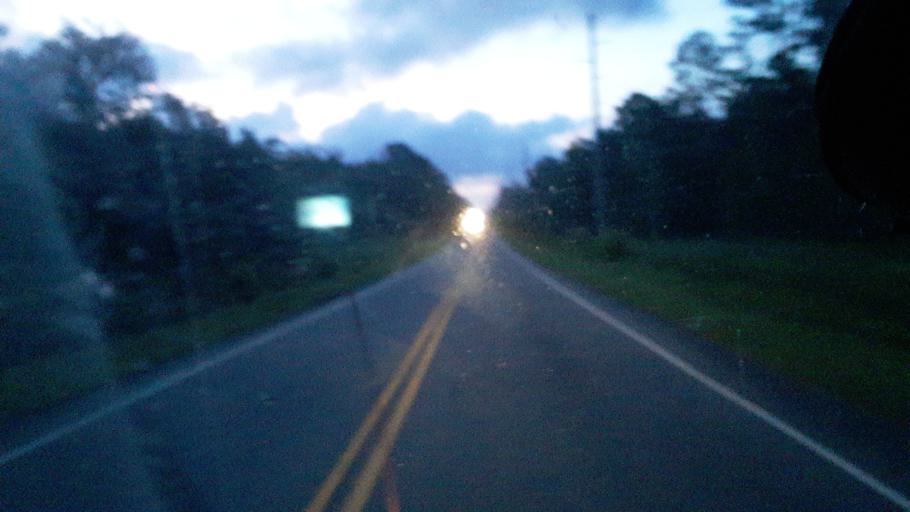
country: US
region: North Carolina
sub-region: Brunswick County
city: Oak Island
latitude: 33.9837
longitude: -78.1794
